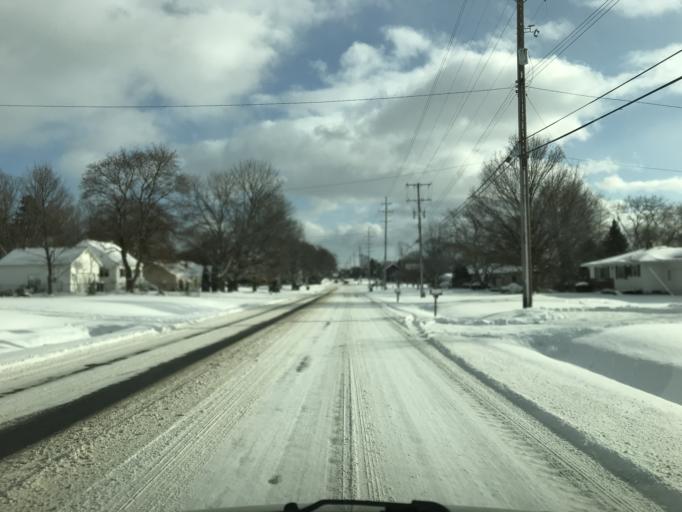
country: US
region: Michigan
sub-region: Kent County
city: Byron Center
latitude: 42.8266
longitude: -85.7061
